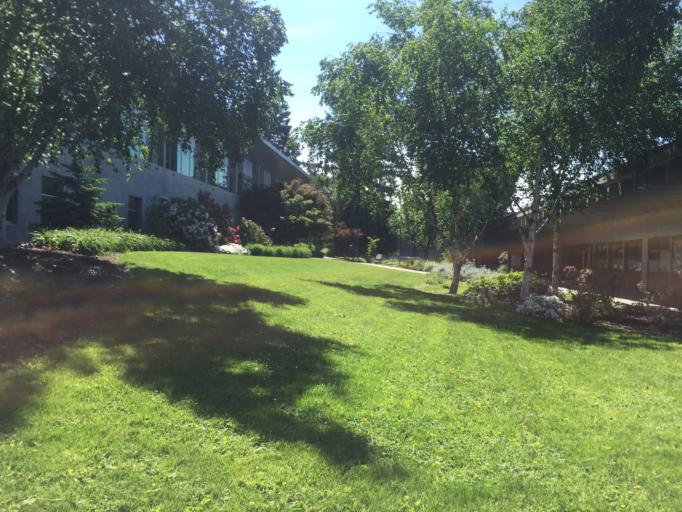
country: US
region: Oregon
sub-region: Washington County
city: Metzger
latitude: 45.4381
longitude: -122.7315
